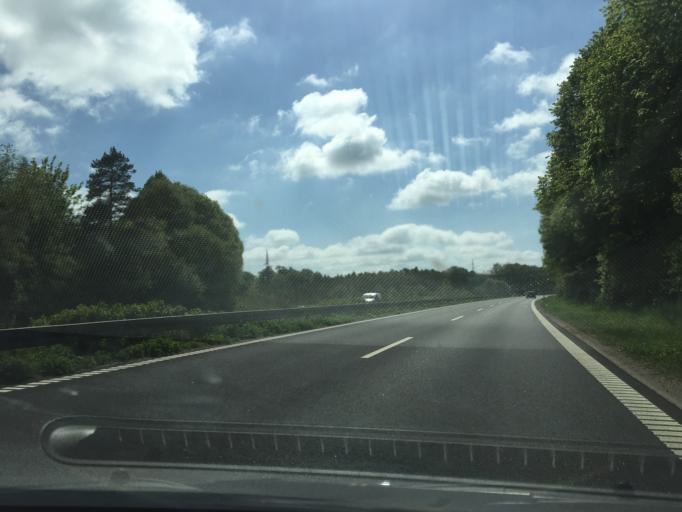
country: DK
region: Zealand
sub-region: Guldborgsund Kommune
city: Sakskobing
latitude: 54.7941
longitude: 11.6587
